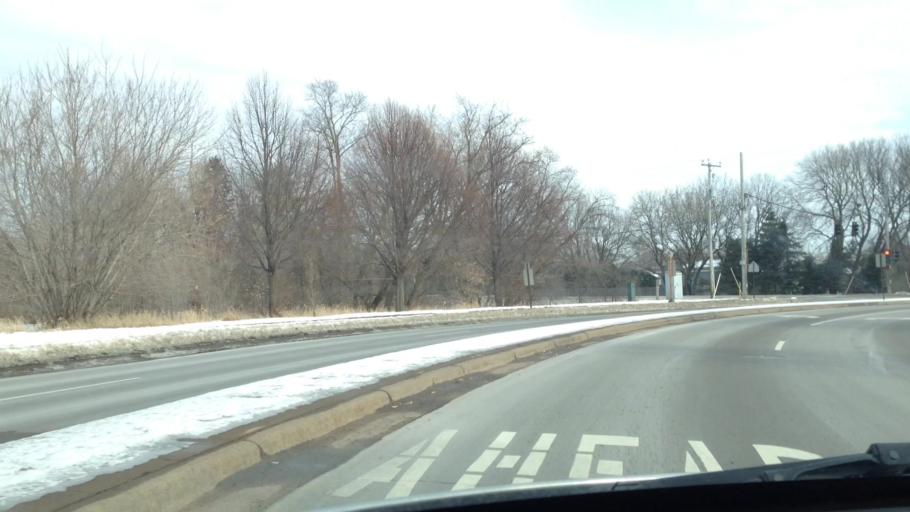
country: US
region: Minnesota
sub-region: Anoka County
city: Lino Lakes
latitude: 45.1686
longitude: -93.1218
